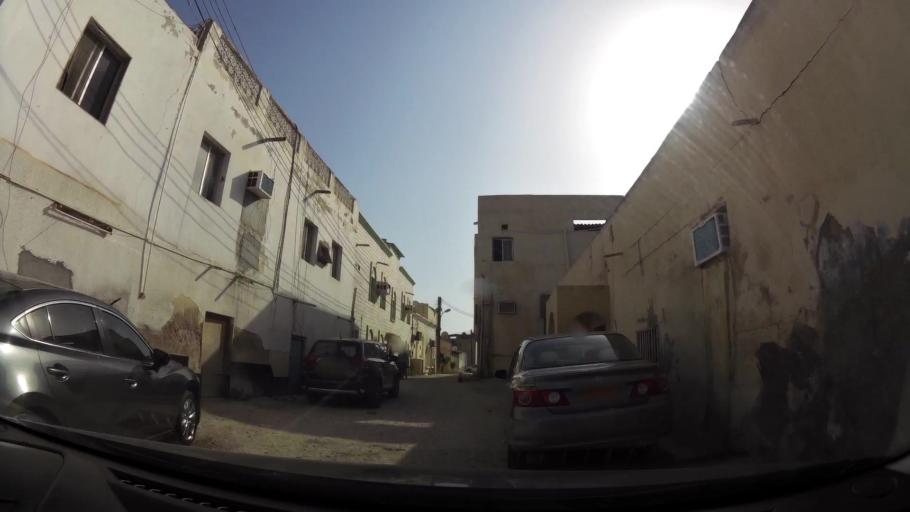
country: OM
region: Zufar
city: Salalah
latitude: 17.0034
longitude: 54.1032
